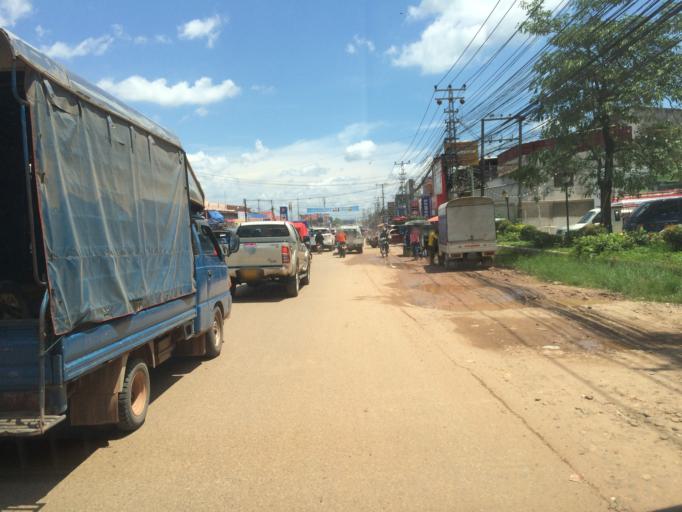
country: TH
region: Nong Khai
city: Si Chiang Mai
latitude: 17.9790
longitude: 102.5551
